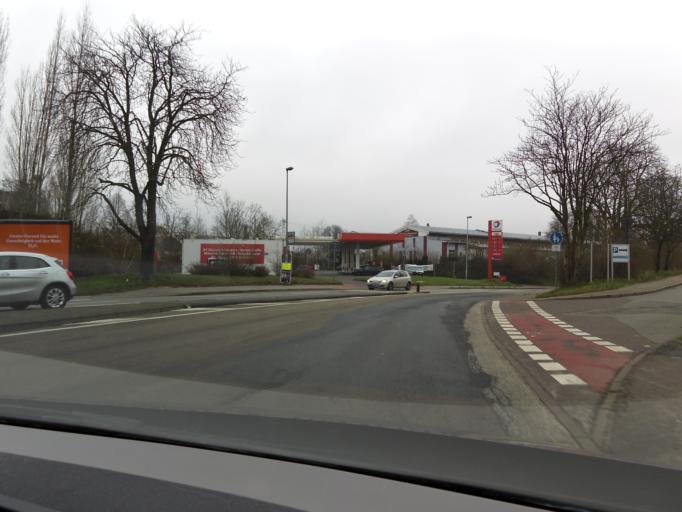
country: DE
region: Mecklenburg-Vorpommern
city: Paulsstadt
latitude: 53.6381
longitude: 11.4034
